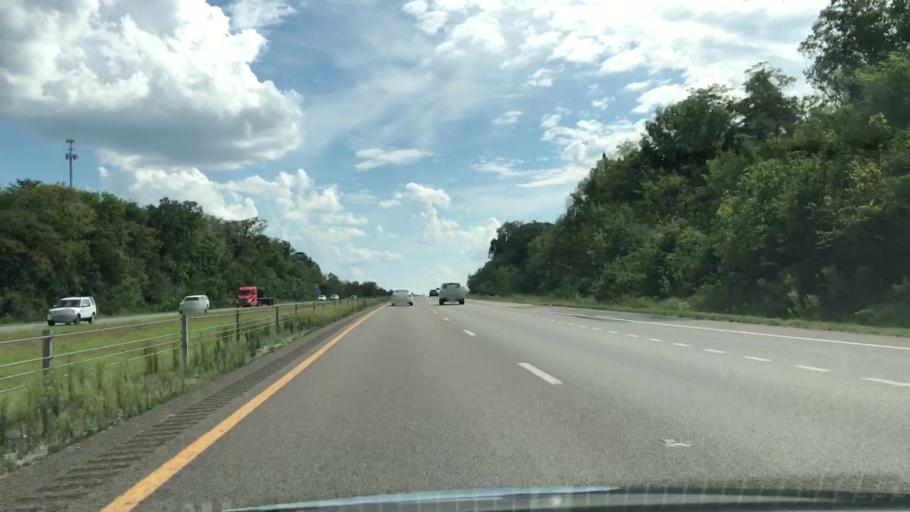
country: US
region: Tennessee
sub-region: Maury County
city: Spring Hill
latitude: 35.6391
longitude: -86.8942
